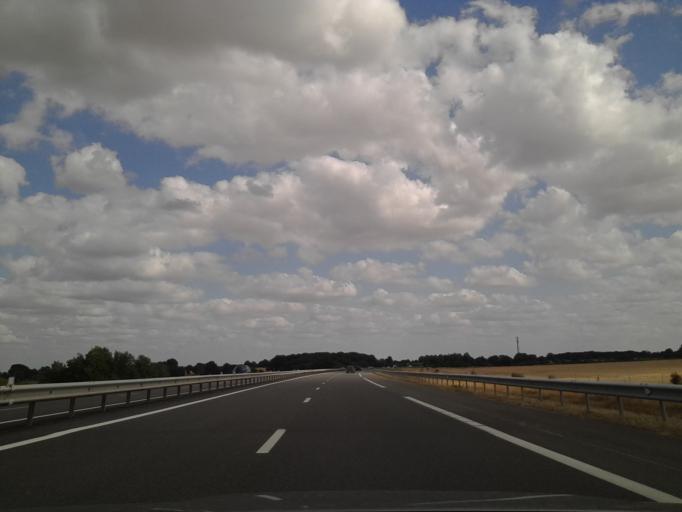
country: FR
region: Centre
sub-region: Departement du Cher
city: Saint-Amand-Montrond
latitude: 46.6385
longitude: 2.4953
